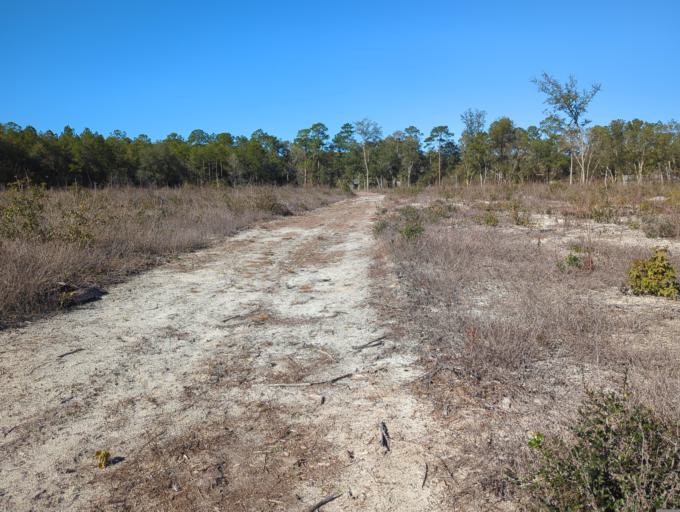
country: US
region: Florida
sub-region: Wakulla County
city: Crawfordville
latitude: 30.1848
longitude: -84.3343
